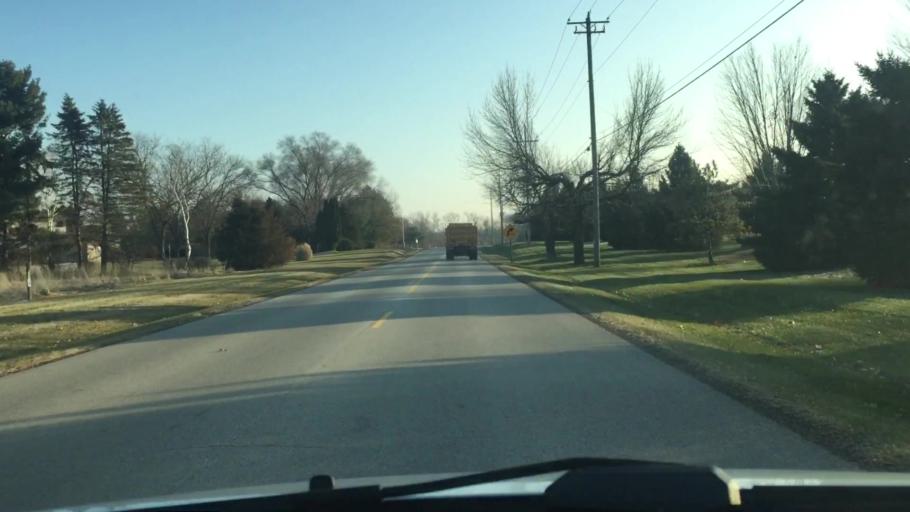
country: US
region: Wisconsin
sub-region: Waukesha County
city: Dousman
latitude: 43.0291
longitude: -88.4791
